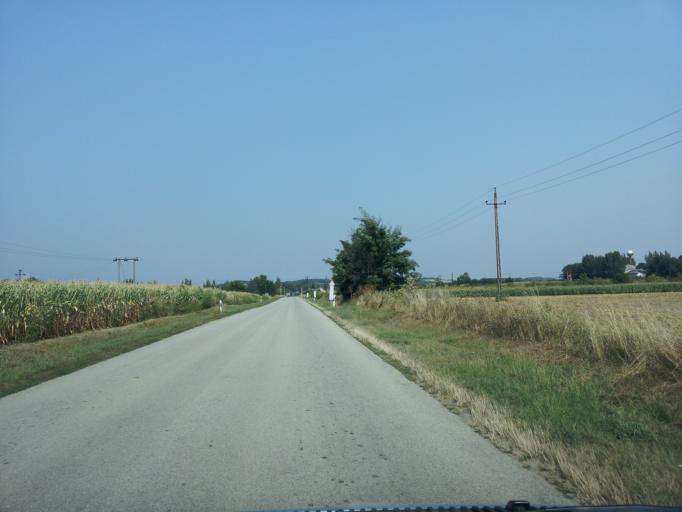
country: HU
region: Gyor-Moson-Sopron
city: Bakonyszentlaszlo
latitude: 47.4375
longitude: 17.7949
